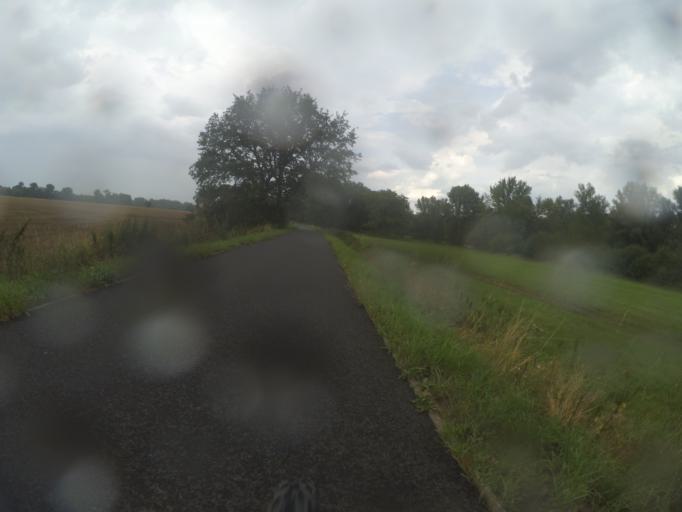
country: CZ
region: Central Bohemia
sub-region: Okres Melnik
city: Melnik
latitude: 50.3281
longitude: 14.4752
